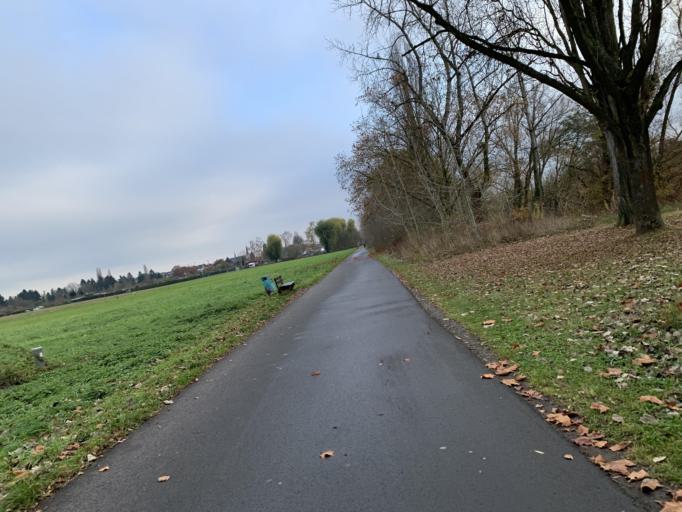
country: DE
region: Hesse
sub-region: Regierungsbezirk Darmstadt
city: Offenbach
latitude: 50.1252
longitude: 8.7720
